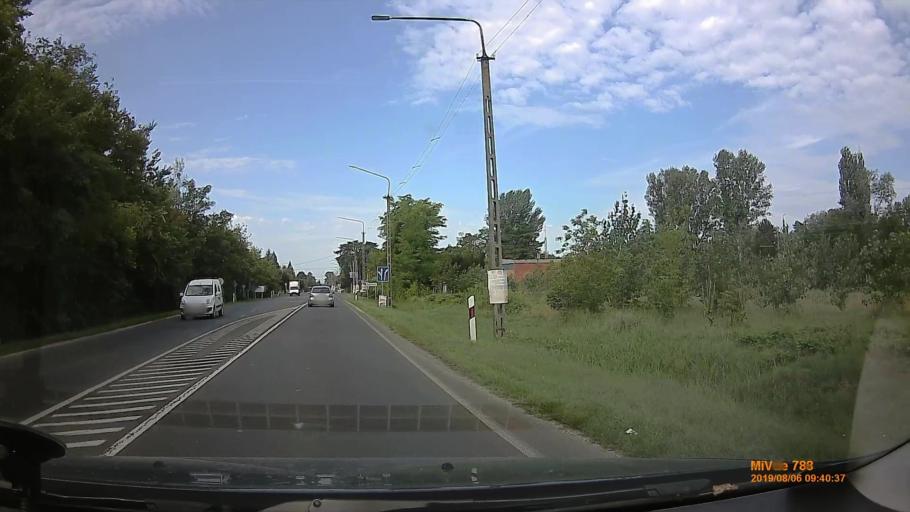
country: HU
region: Somogy
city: Balatonlelle
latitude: 46.7963
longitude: 17.7279
